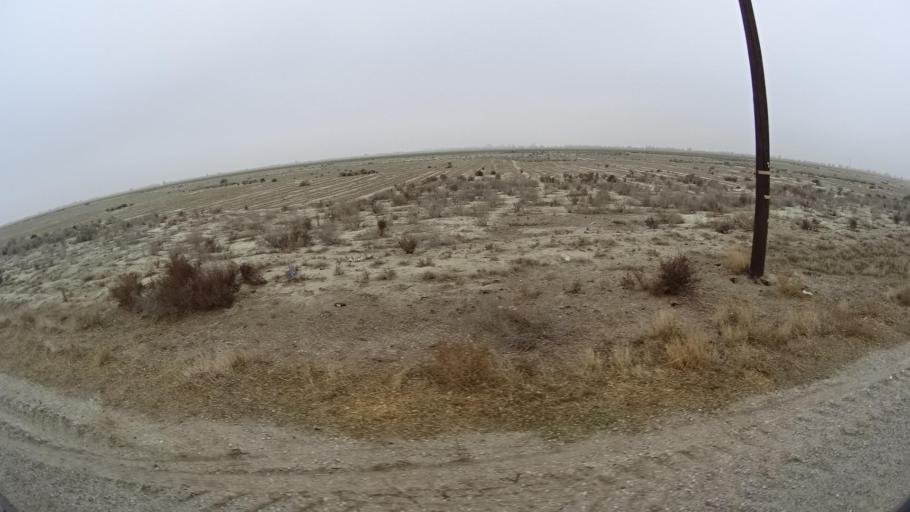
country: US
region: California
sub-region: Kern County
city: Rosedale
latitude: 35.2276
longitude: -119.2328
